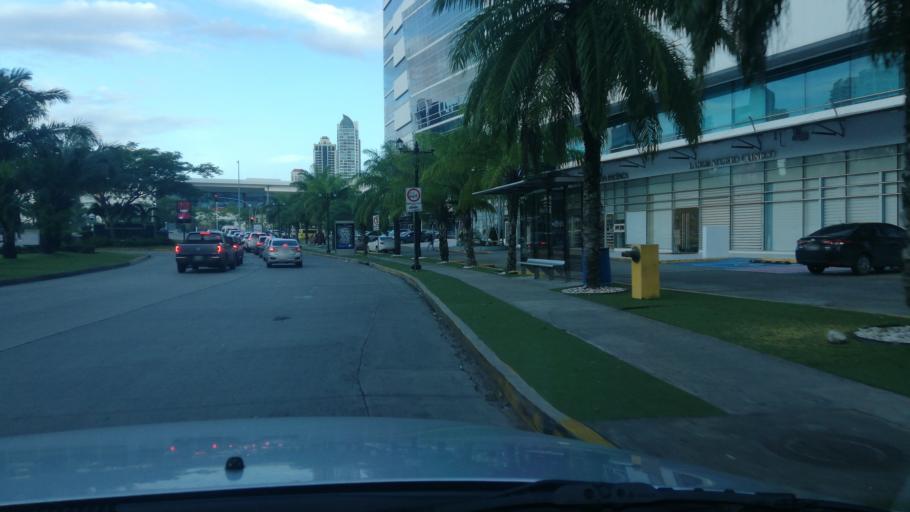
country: PA
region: Panama
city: Panama
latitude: 8.9816
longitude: -79.5106
